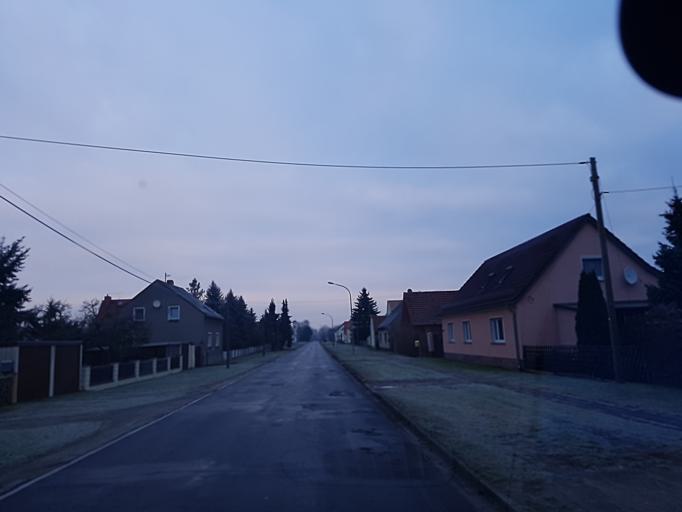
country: DE
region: Brandenburg
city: Finsterwalde
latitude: 51.6594
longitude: 13.7122
